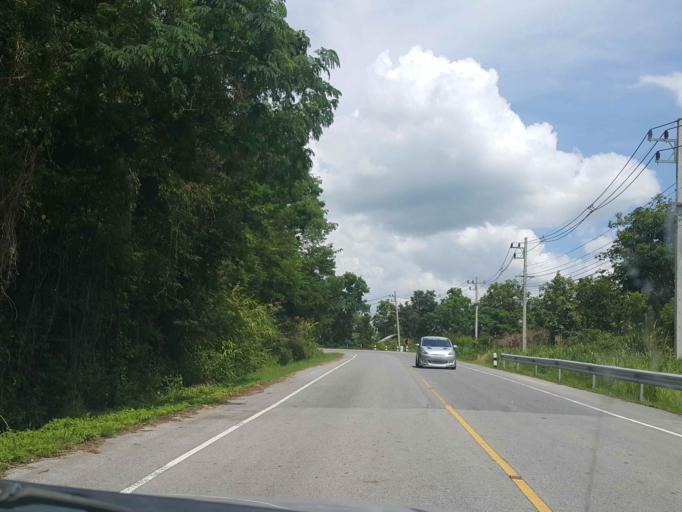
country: TH
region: Nan
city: Ban Luang
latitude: 18.8740
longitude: 100.4888
